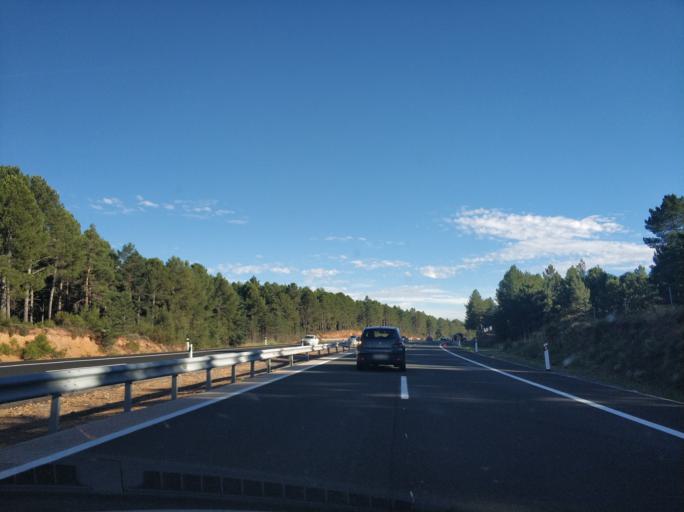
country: ES
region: Castille and Leon
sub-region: Provincia de Leon
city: Cimanes del Tejar
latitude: 42.6760
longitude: -5.7498
